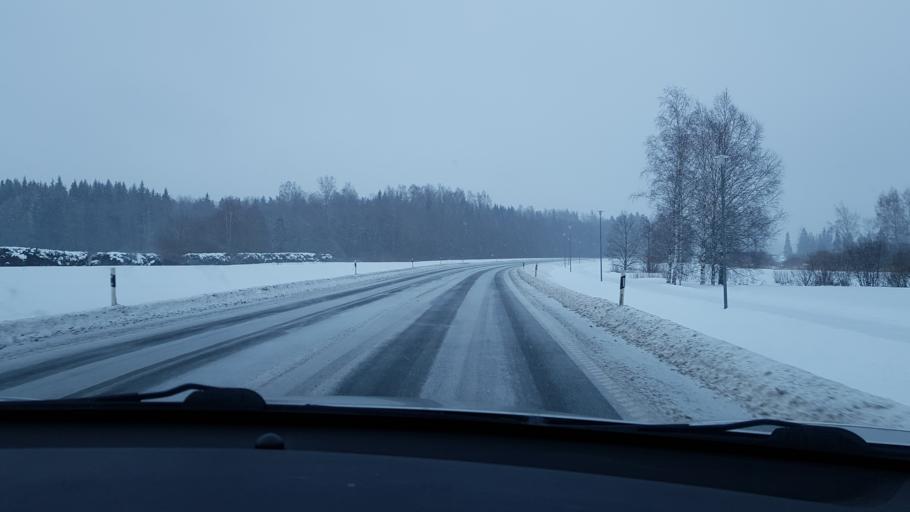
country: EE
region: Jaervamaa
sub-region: Tueri vald
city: Tueri
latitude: 58.8286
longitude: 25.4599
